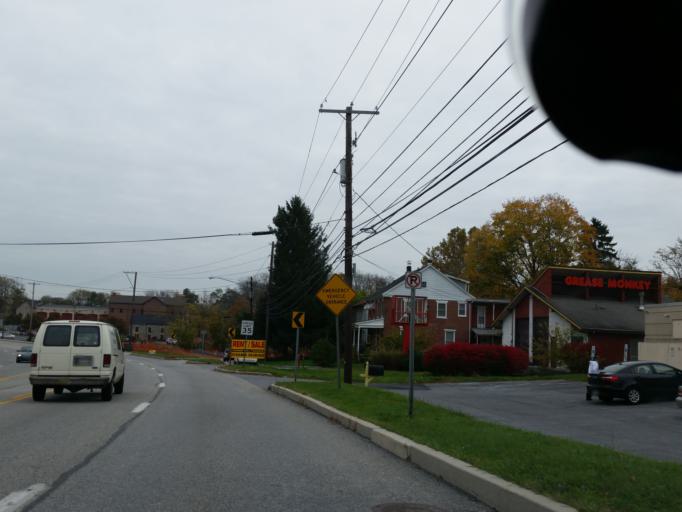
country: US
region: Pennsylvania
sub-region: Cumberland County
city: Camp Hill
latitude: 40.2287
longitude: -76.9221
